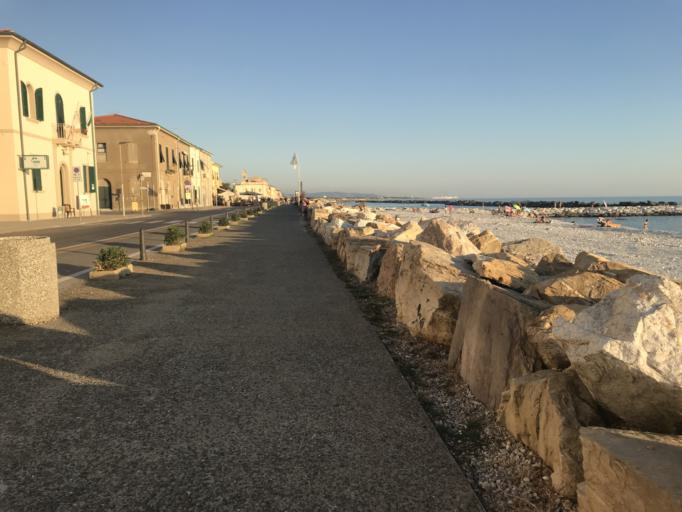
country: IT
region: Tuscany
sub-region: Province of Pisa
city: Marina di Pisa
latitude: 43.6650
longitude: 10.2765
